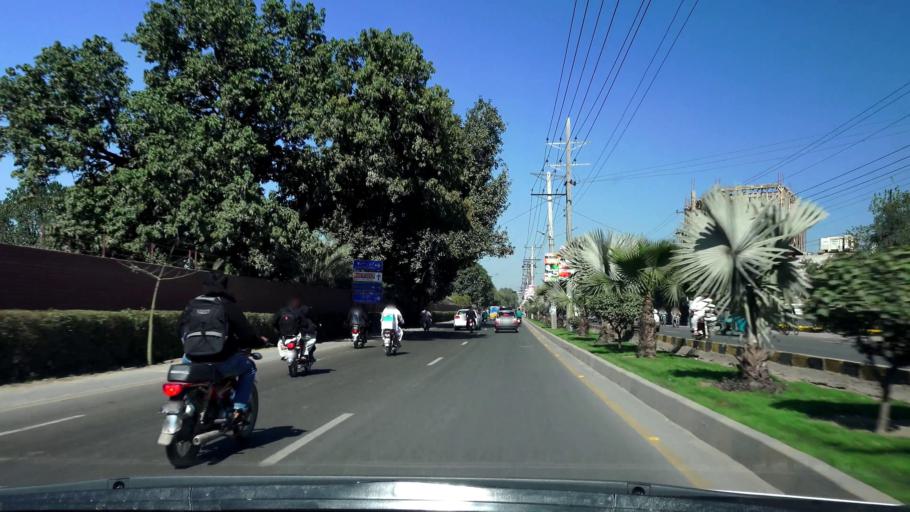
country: PK
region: Punjab
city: Faisalabad
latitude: 31.4328
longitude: 73.0784
